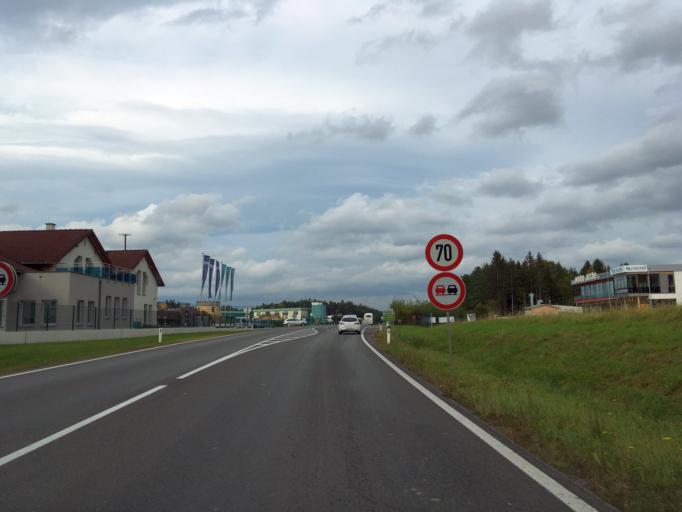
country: AT
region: Styria
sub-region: Politischer Bezirk Hartberg-Fuerstenfeld
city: Hartberg
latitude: 47.3142
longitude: 15.9820
